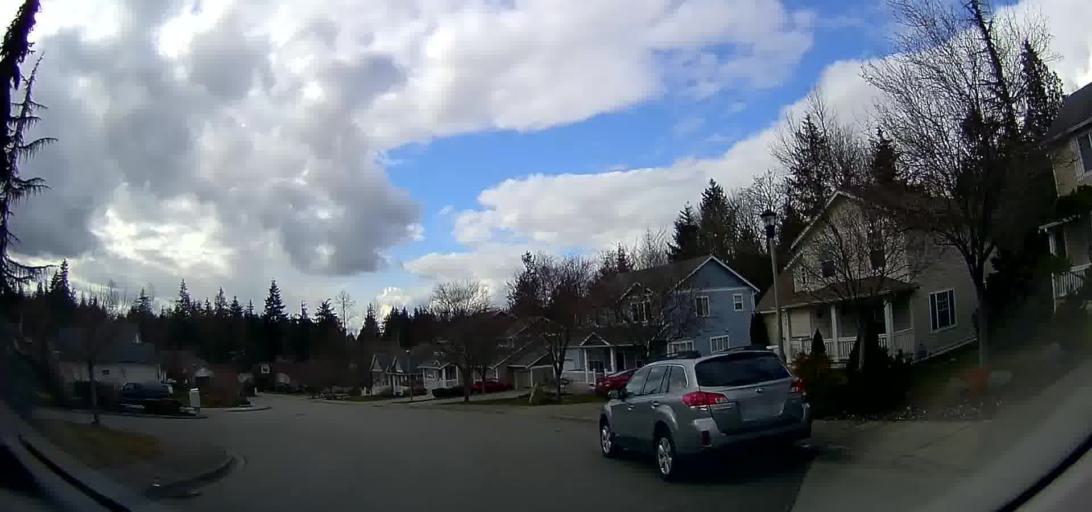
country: US
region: Washington
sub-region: Skagit County
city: Mount Vernon
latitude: 48.4128
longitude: -122.2881
